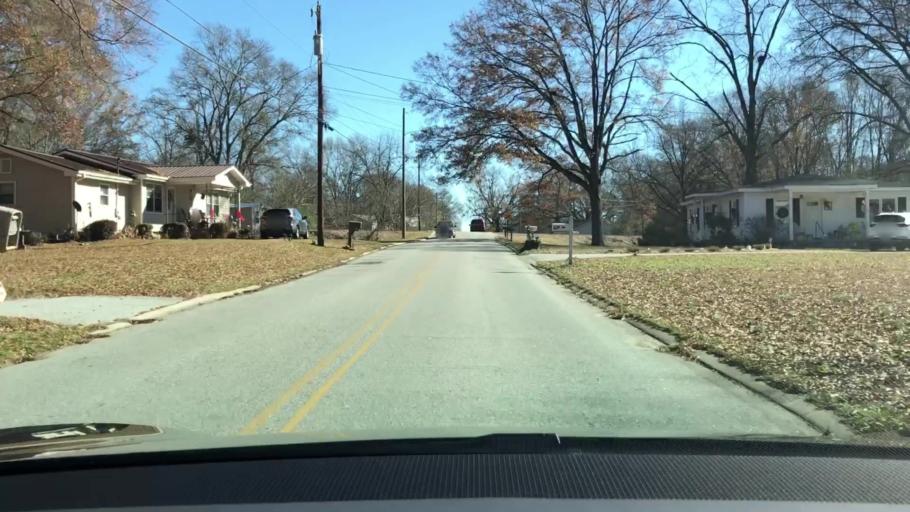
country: US
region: Georgia
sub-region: Walton County
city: Monroe
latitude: 33.7779
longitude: -83.7031
